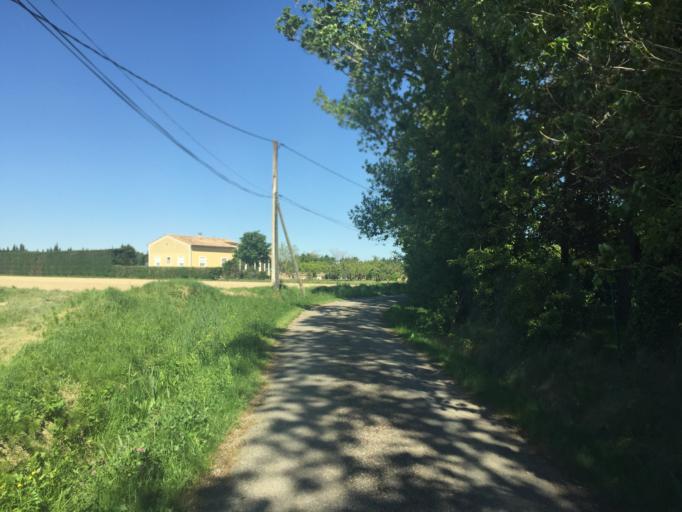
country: FR
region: Provence-Alpes-Cote d'Azur
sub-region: Departement du Vaucluse
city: Orange
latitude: 44.1397
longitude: 4.7834
